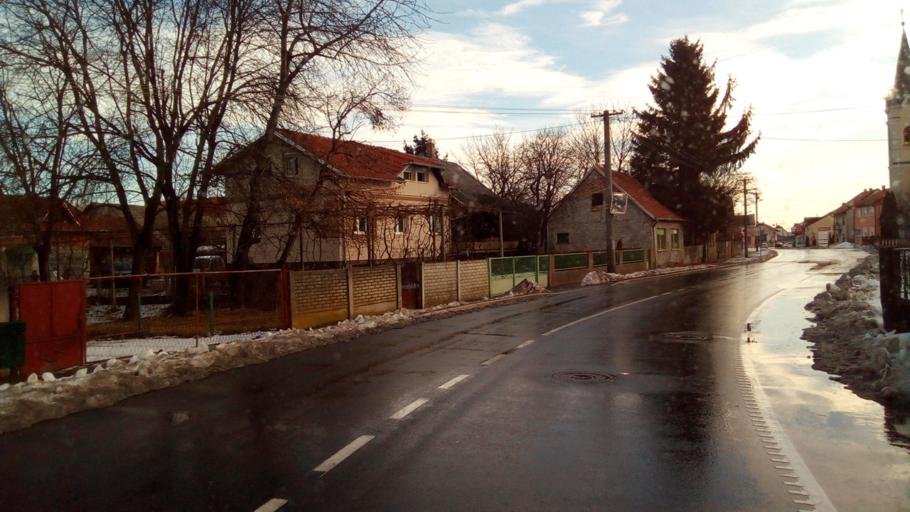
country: HR
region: Medimurska
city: Pribislavec
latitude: 46.3944
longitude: 16.4748
